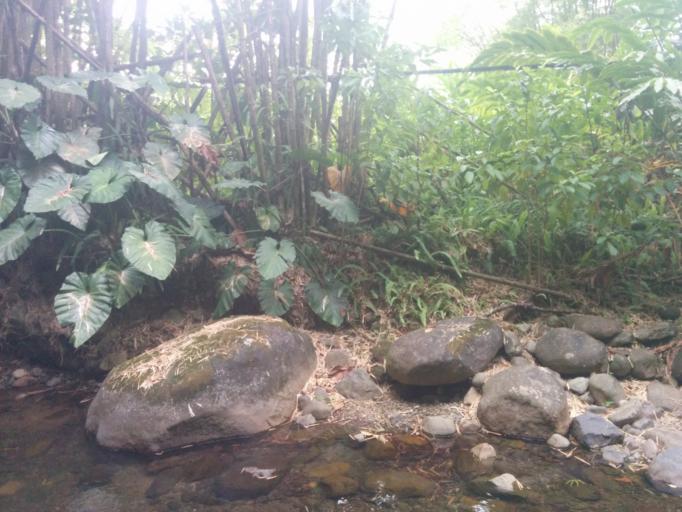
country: GP
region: Guadeloupe
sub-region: Guadeloupe
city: Capesterre-Belle-Eau
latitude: 16.1061
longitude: -61.6079
